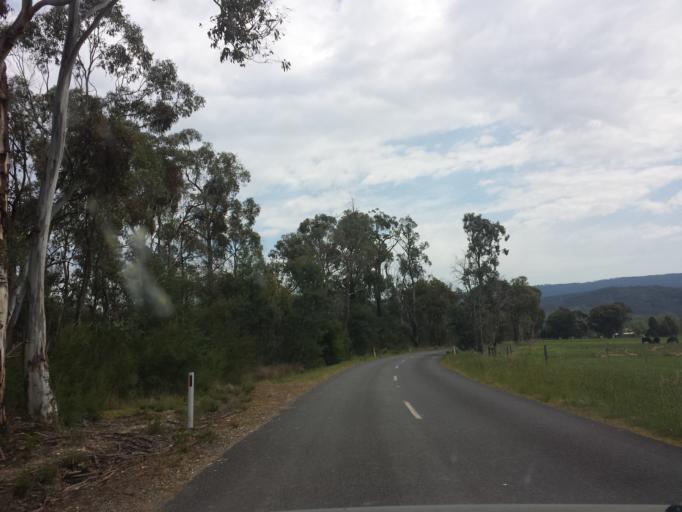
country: AU
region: Victoria
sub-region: Murrindindi
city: Alexandra
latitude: -37.3413
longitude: 145.7304
